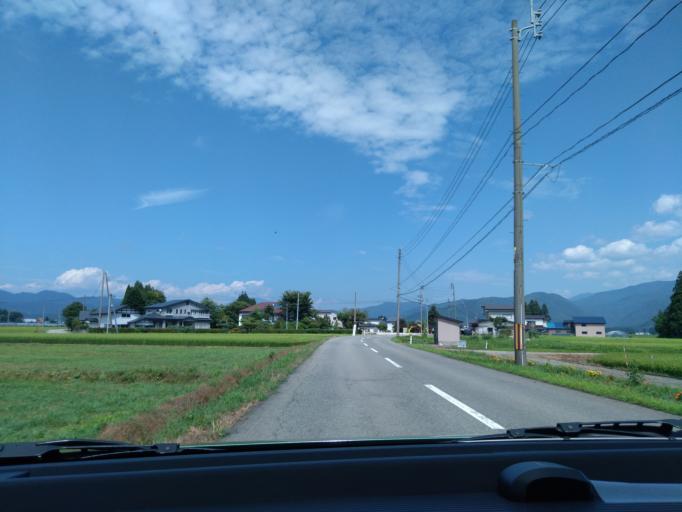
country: JP
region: Akita
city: Kakunodatemachi
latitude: 39.6043
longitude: 140.5894
